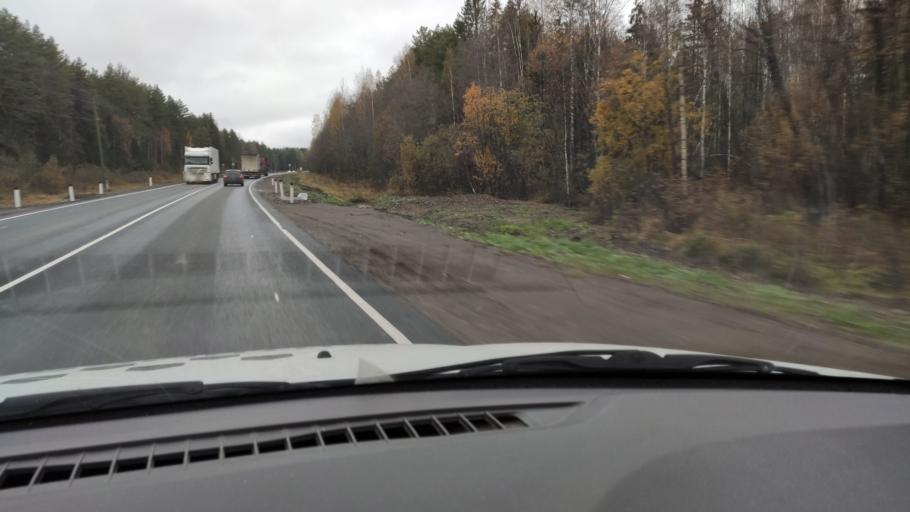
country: RU
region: Kirov
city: Belaya Kholunitsa
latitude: 58.8427
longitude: 50.7717
